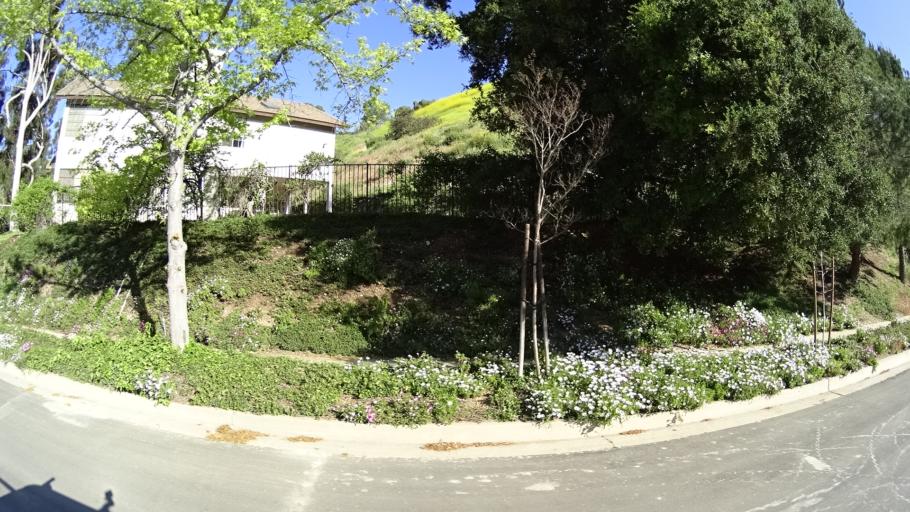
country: US
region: California
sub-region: Ventura County
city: Thousand Oaks
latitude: 34.1912
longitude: -118.8346
